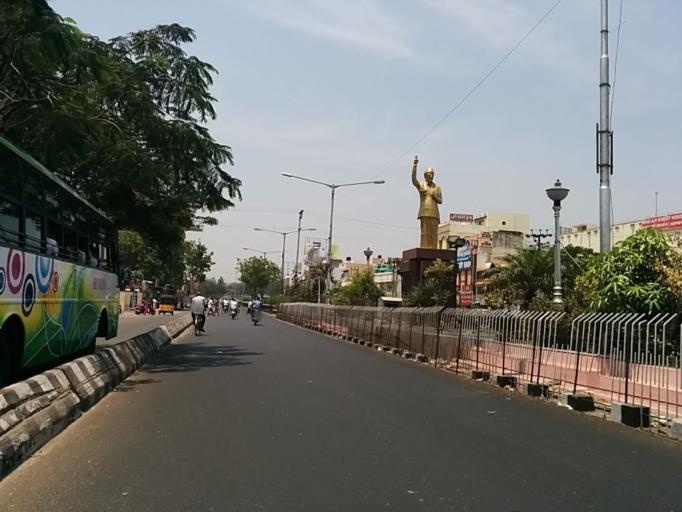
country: IN
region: Pondicherry
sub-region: Puducherry
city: Puducherry
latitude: 11.9320
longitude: 79.8153
